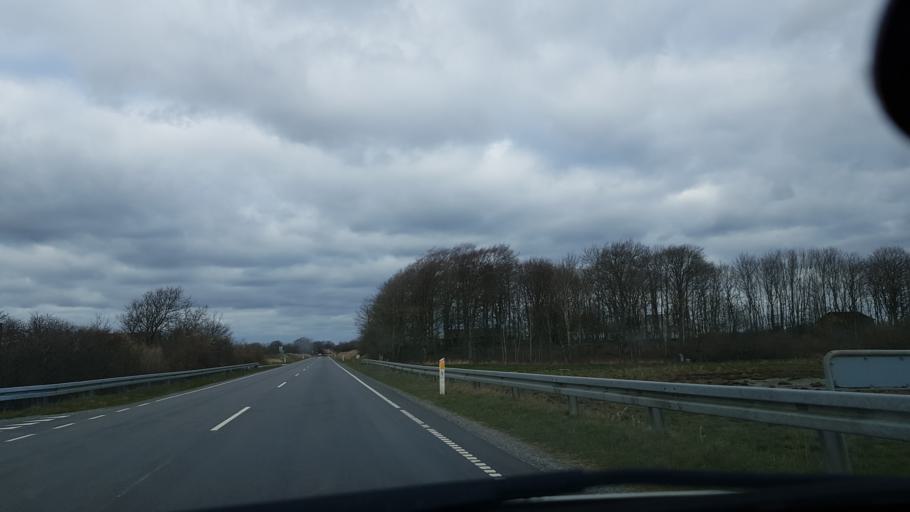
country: DK
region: South Denmark
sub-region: Vejen Kommune
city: Holsted
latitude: 55.4079
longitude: 8.8854
